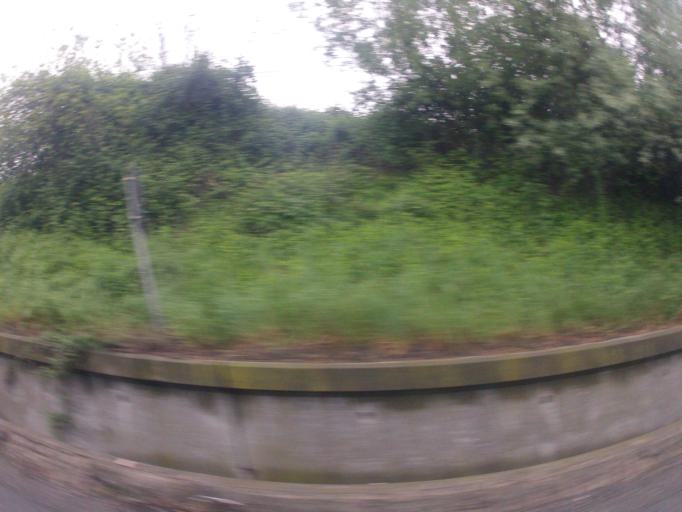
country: IT
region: Piedmont
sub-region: Provincia di Torino
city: La Loggia
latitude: 44.9455
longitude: 7.6785
